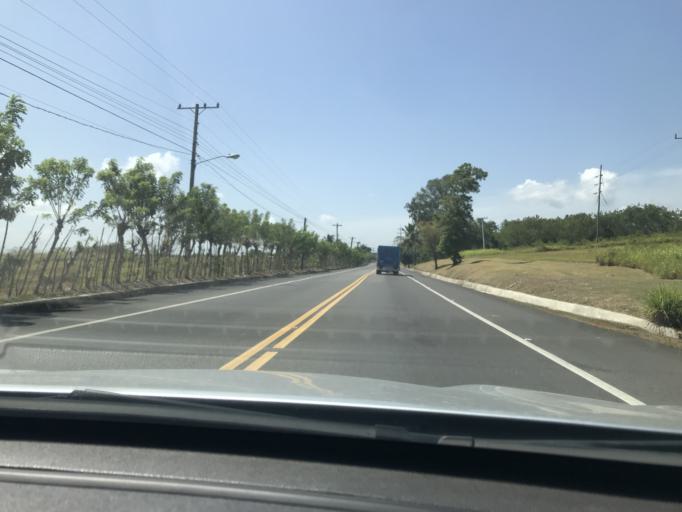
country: DO
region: Puerto Plata
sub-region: Puerto Plata
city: Puerto Plata
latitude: 19.7344
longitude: -70.6290
